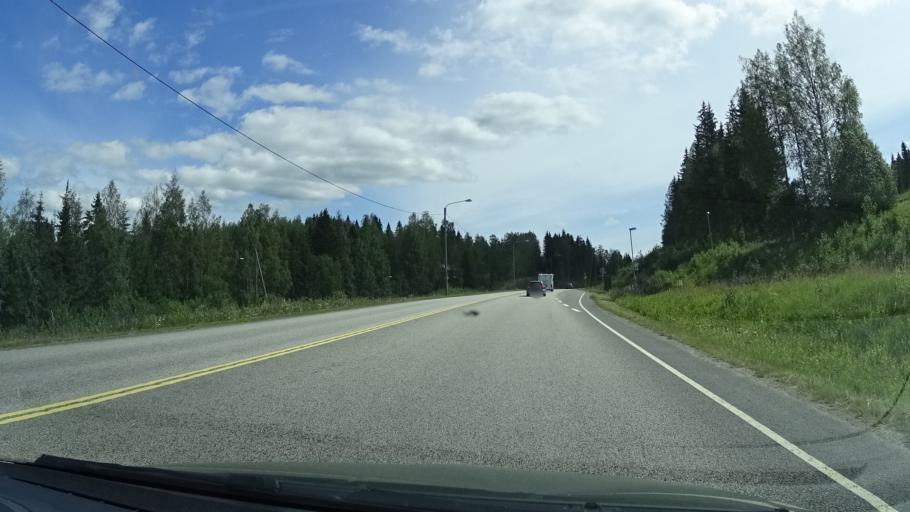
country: FI
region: Central Finland
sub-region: Jyvaeskylae
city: Jyvaeskylae
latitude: 62.2649
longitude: 25.5792
